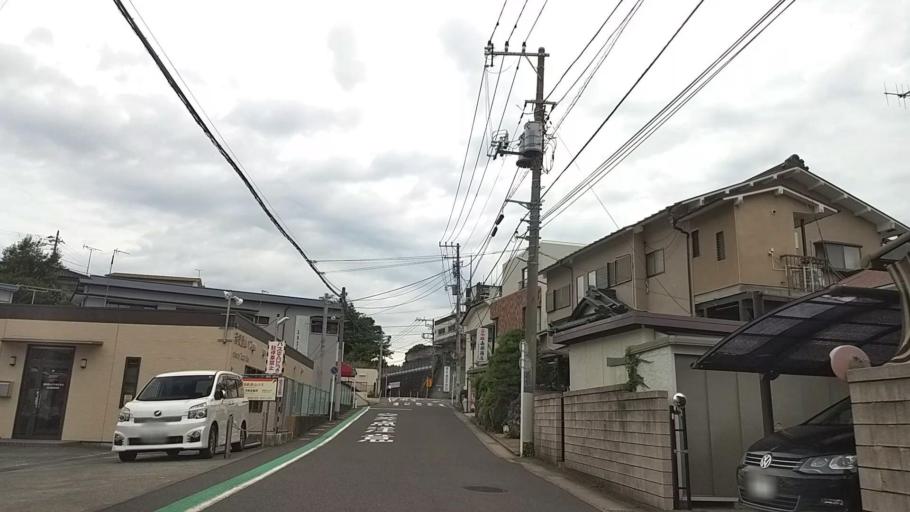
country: JP
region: Kanagawa
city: Yugawara
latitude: 35.1472
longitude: 139.1071
